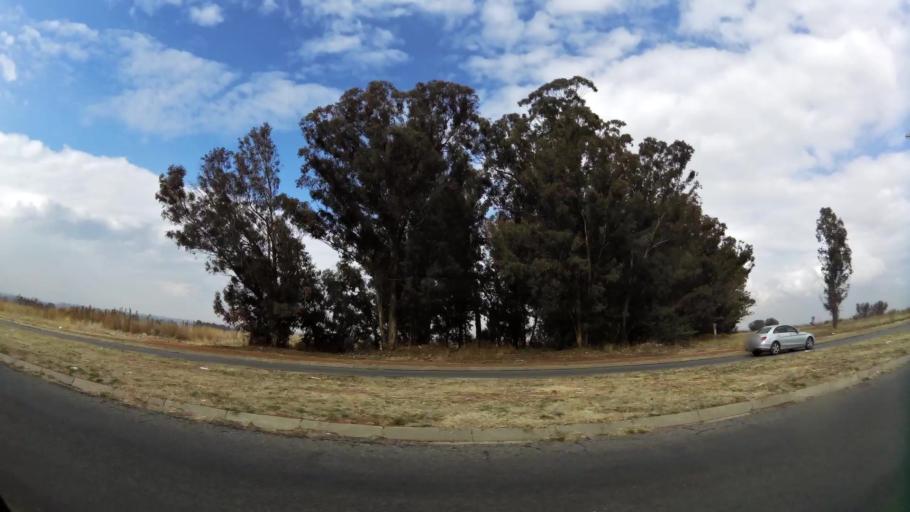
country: ZA
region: Gauteng
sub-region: Sedibeng District Municipality
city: Vanderbijlpark
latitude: -26.7278
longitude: 27.8736
